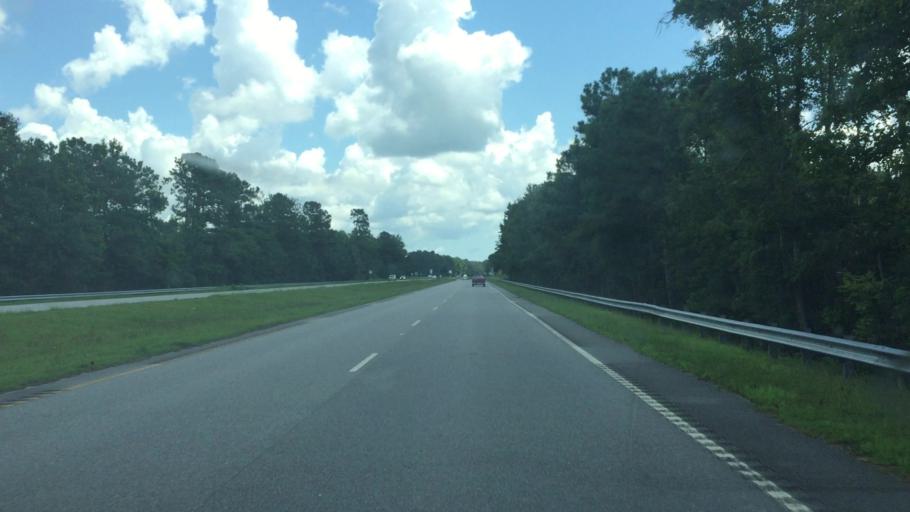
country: US
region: South Carolina
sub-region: Horry County
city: Loris
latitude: 34.0370
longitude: -78.8143
